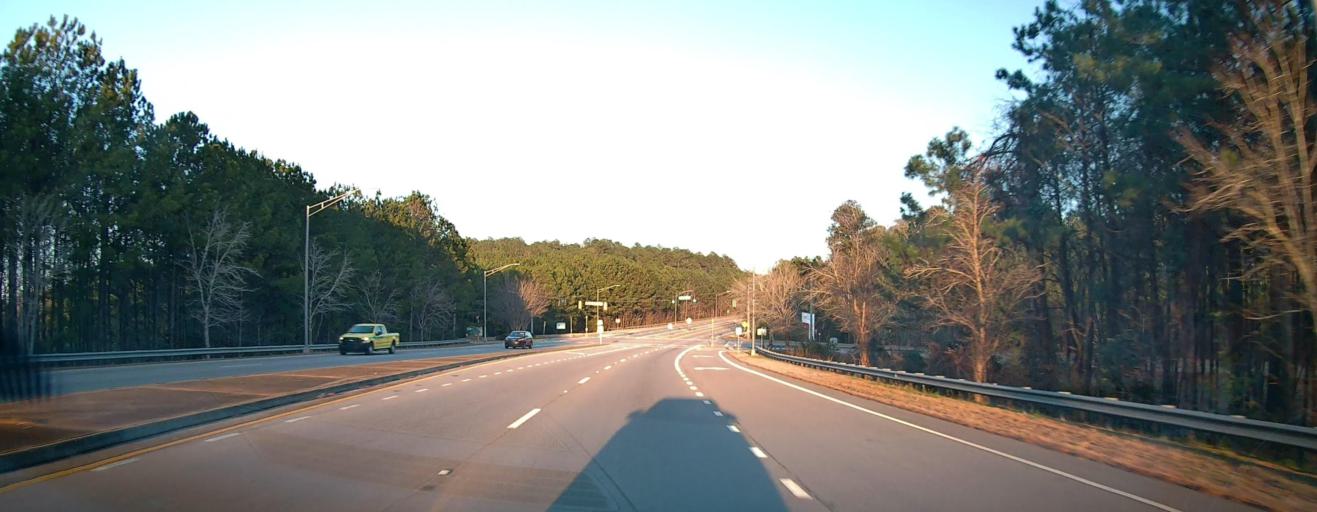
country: US
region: Georgia
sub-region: Troup County
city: La Grange
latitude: 33.0337
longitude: -85.0631
